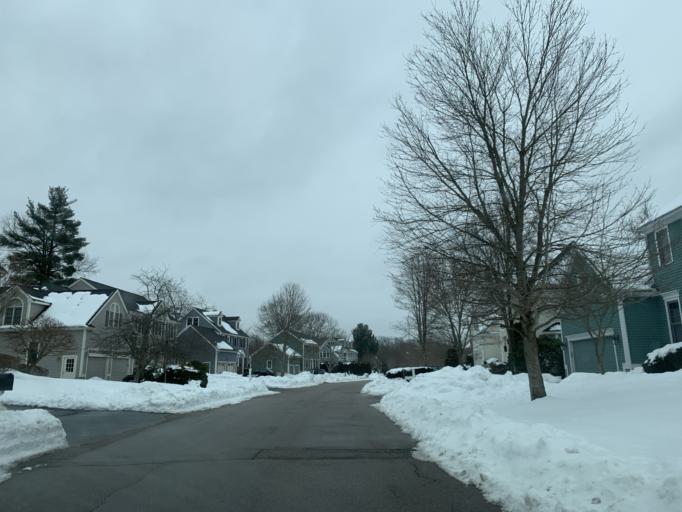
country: US
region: Massachusetts
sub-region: Norfolk County
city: Westwood
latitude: 42.2031
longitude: -71.2246
